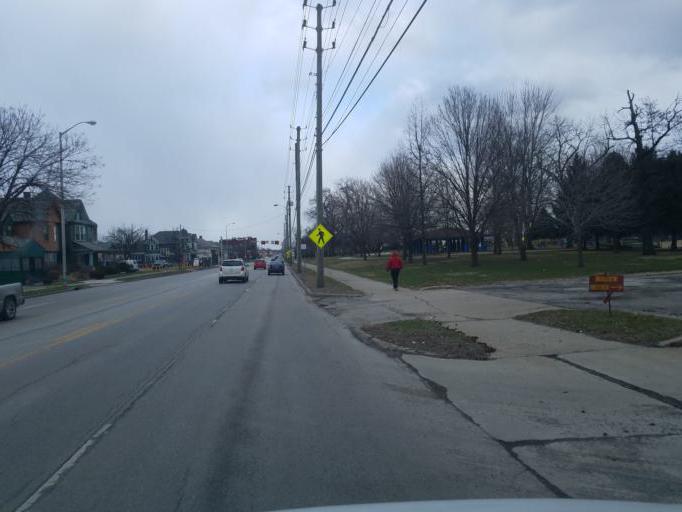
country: US
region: Indiana
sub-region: Marion County
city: Indianapolis
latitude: 39.7673
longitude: -86.1300
